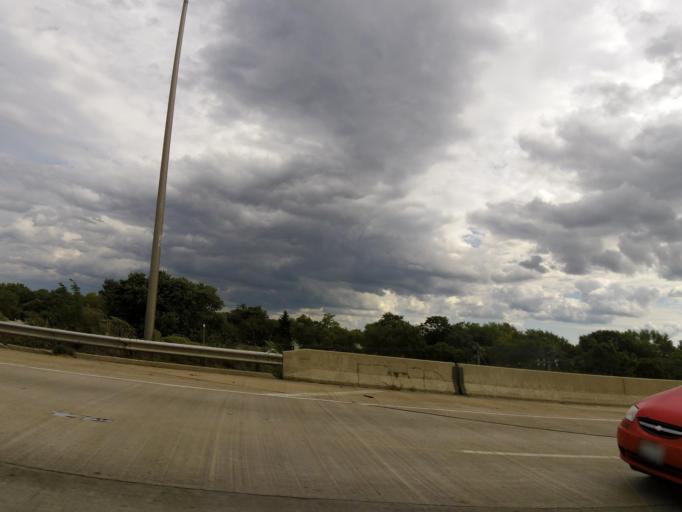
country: US
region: Illinois
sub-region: Cook County
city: Country Club Hills
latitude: 41.5719
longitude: -87.7296
